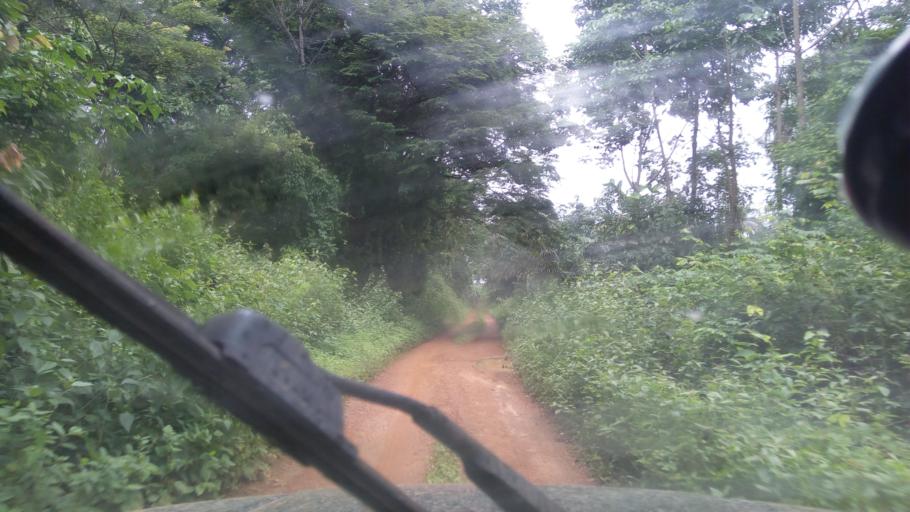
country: SL
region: Eastern Province
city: Gorahun
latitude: 7.6231
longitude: -11.2630
